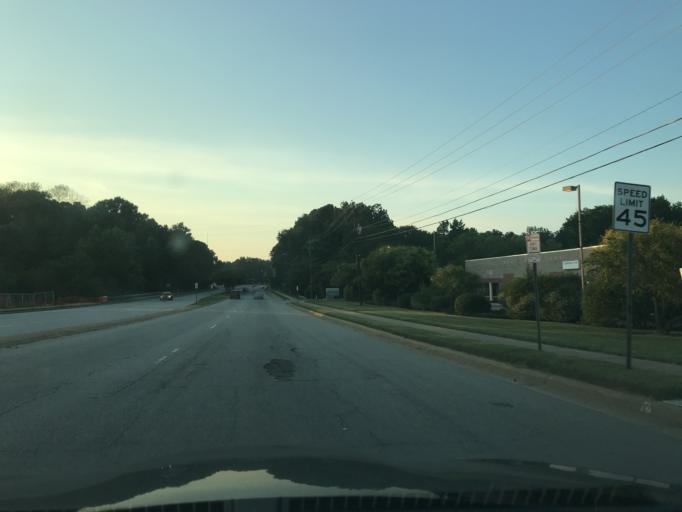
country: US
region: North Carolina
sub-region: Wake County
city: Raleigh
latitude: 35.7611
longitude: -78.6137
